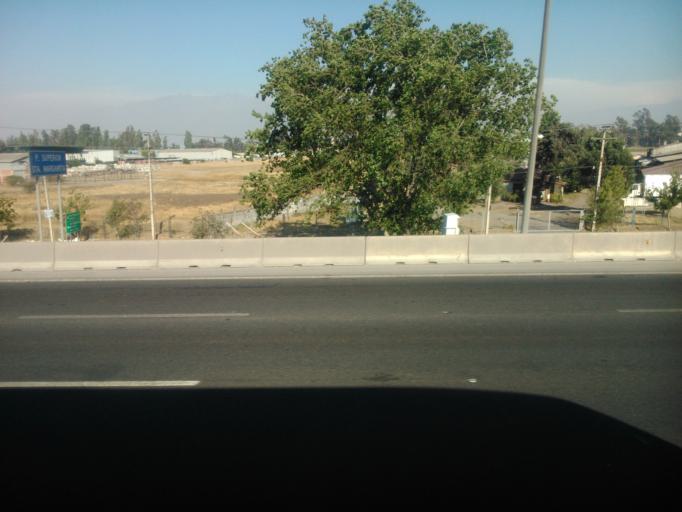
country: CL
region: Santiago Metropolitan
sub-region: Provincia de Maipo
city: San Bernardo
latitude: -33.5449
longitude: -70.7083
